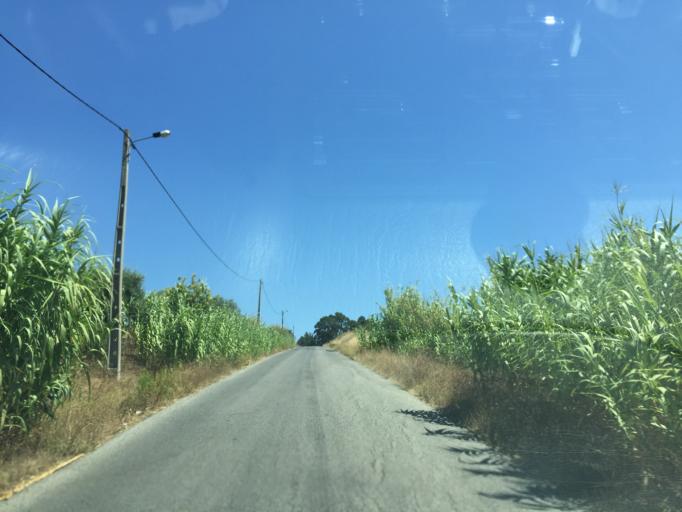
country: PT
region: Lisbon
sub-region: Azambuja
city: Aveiras de Cima
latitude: 39.1513
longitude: -8.8885
